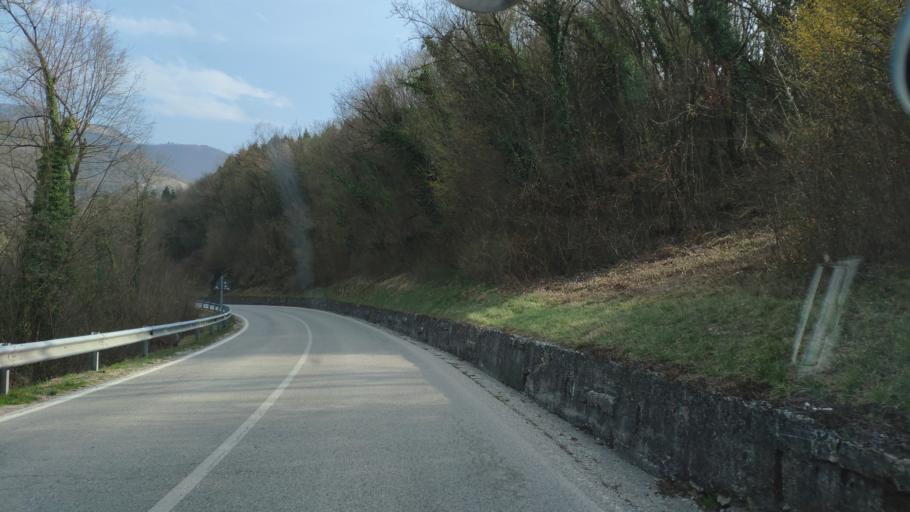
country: IT
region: Veneto
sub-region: Provincia di Vicenza
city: Enego
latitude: 45.9492
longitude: 11.7206
